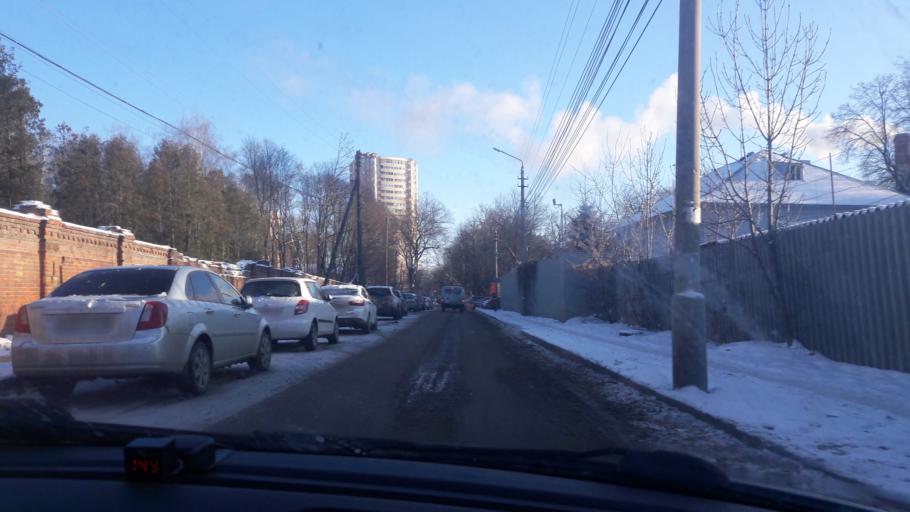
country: RU
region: Tula
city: Tula
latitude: 54.1764
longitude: 37.6081
